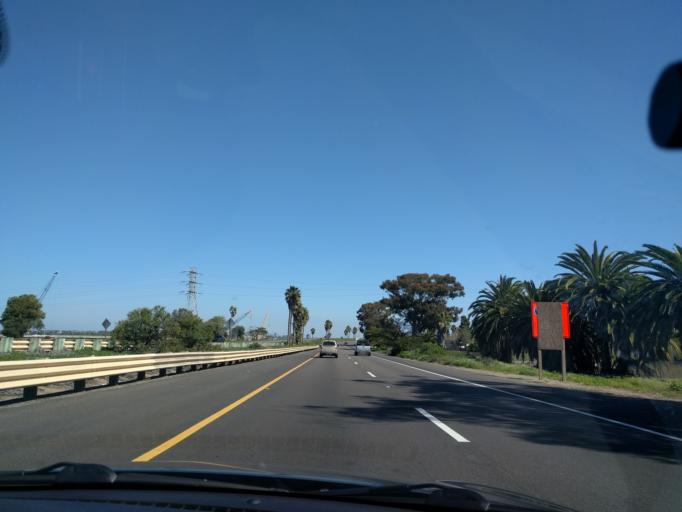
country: US
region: California
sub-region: San Diego County
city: San Diego
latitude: 32.7564
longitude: -117.2296
